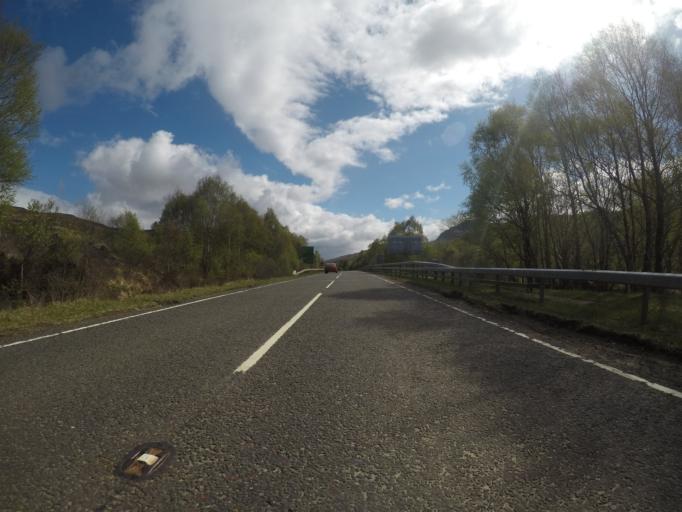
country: GB
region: Scotland
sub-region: Highland
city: Spean Bridge
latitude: 57.1455
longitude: -4.9627
